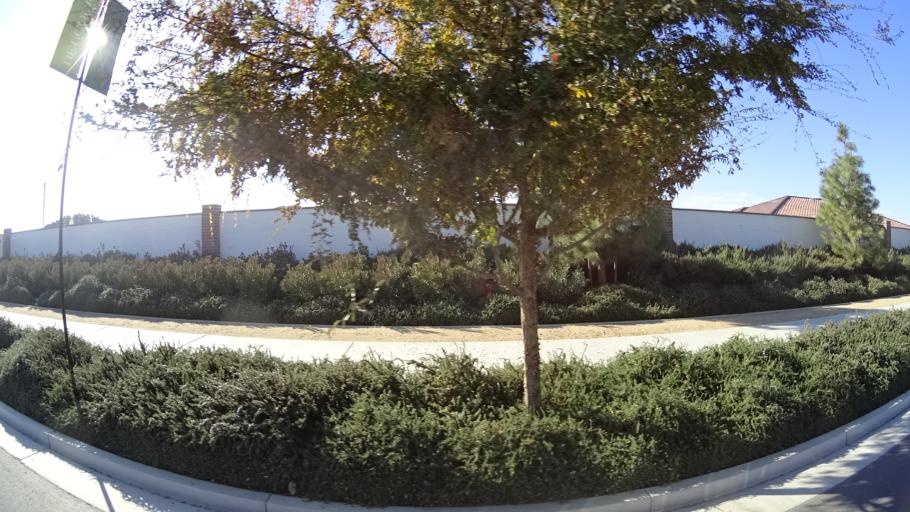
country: US
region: California
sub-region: Kern County
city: Rosedale
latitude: 35.3232
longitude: -119.1368
